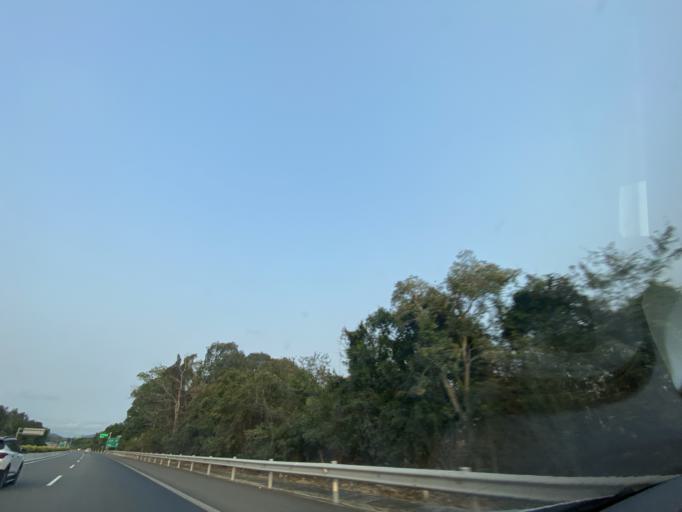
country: CN
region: Hainan
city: Yingzhou
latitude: 18.4317
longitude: 109.8410
